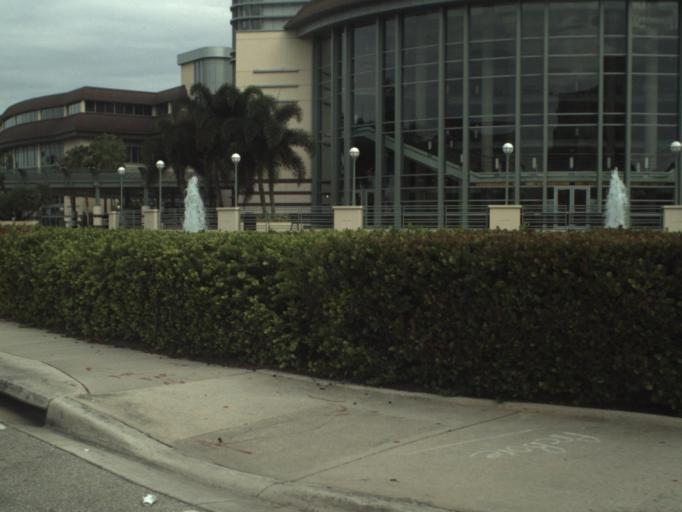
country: US
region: Florida
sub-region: Palm Beach County
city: West Palm Beach
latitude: 26.7062
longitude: -80.0590
